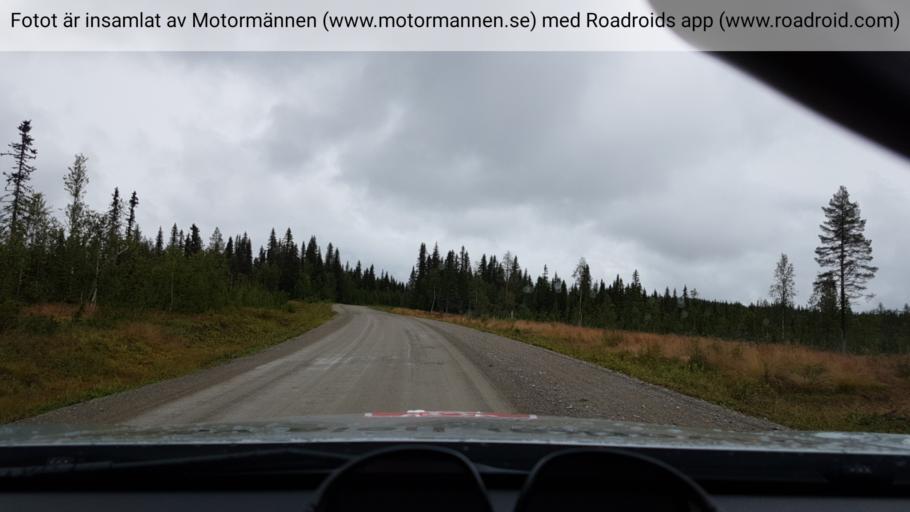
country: SE
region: Vaesterbotten
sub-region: Storumans Kommun
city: Storuman
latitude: 64.8532
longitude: 17.4021
